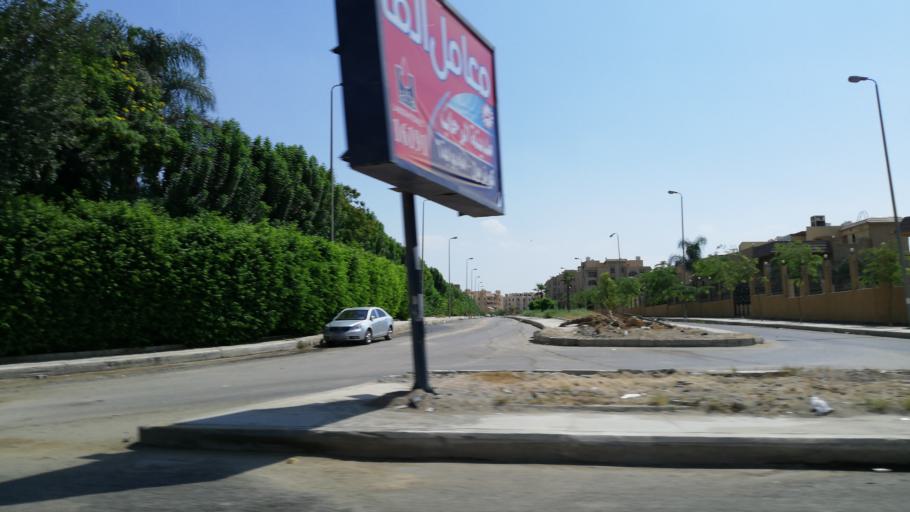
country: EG
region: Muhafazat al Qalyubiyah
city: Al Khankah
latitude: 30.0532
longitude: 31.4942
